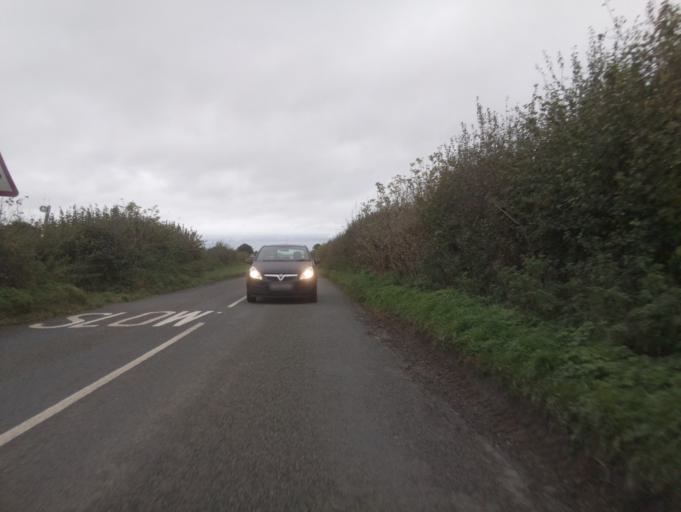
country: GB
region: England
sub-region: Dorset
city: Sherborne
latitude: 50.9734
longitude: -2.5571
